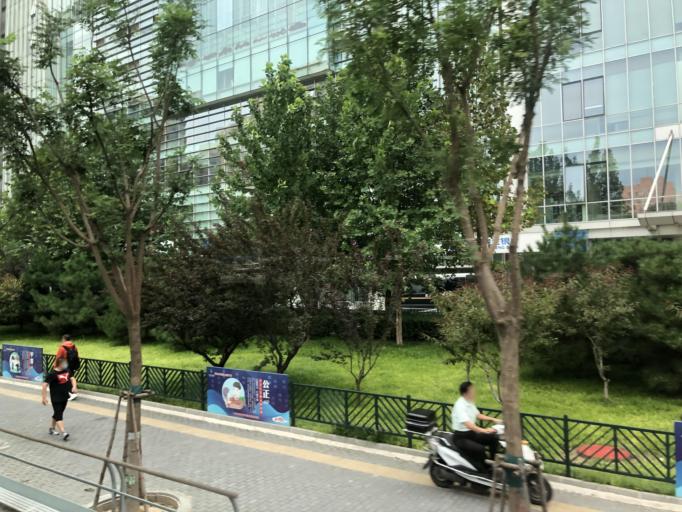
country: CN
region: Beijing
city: Jinrongjie
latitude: 39.9340
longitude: 116.3190
